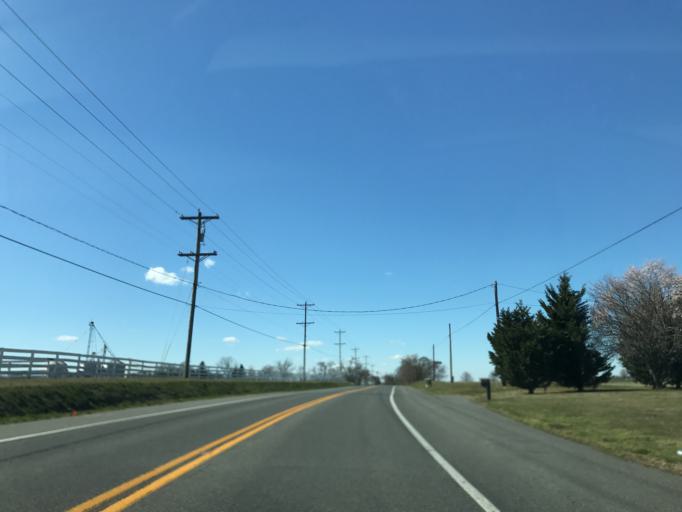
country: US
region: Maryland
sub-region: Kent County
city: Chestertown
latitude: 39.2111
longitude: -76.1021
